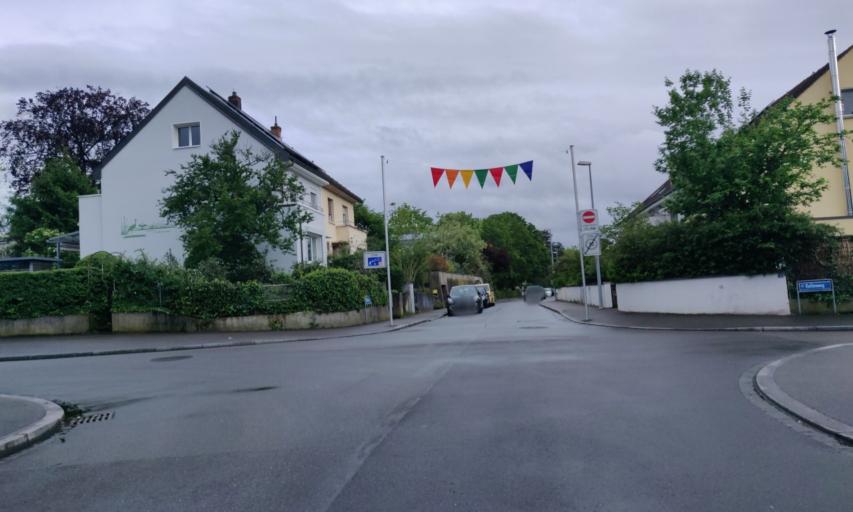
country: CH
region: Basel-City
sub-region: Basel-Stadt
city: Riehen
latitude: 47.5734
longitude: 7.6349
